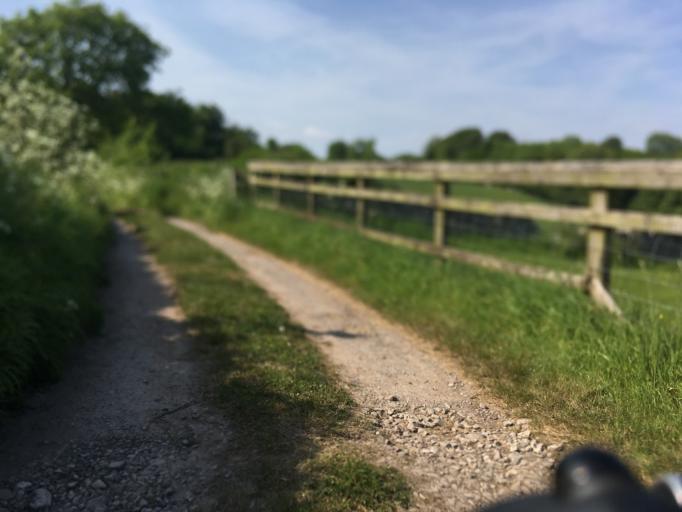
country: GB
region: England
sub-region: South Gloucestershire
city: Falfield
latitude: 51.6168
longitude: -2.4509
